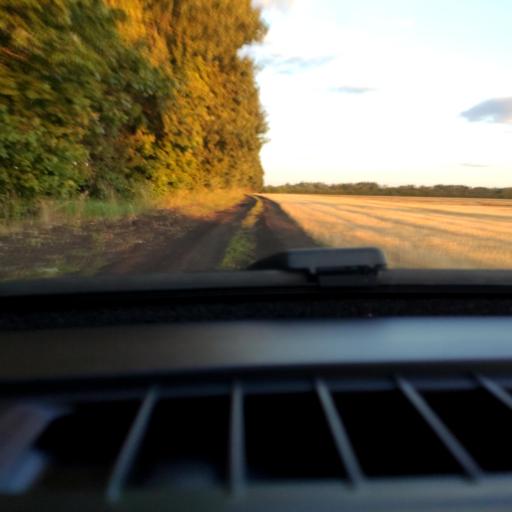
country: RU
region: Voronezj
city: Panino
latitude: 51.5703
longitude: 39.8828
